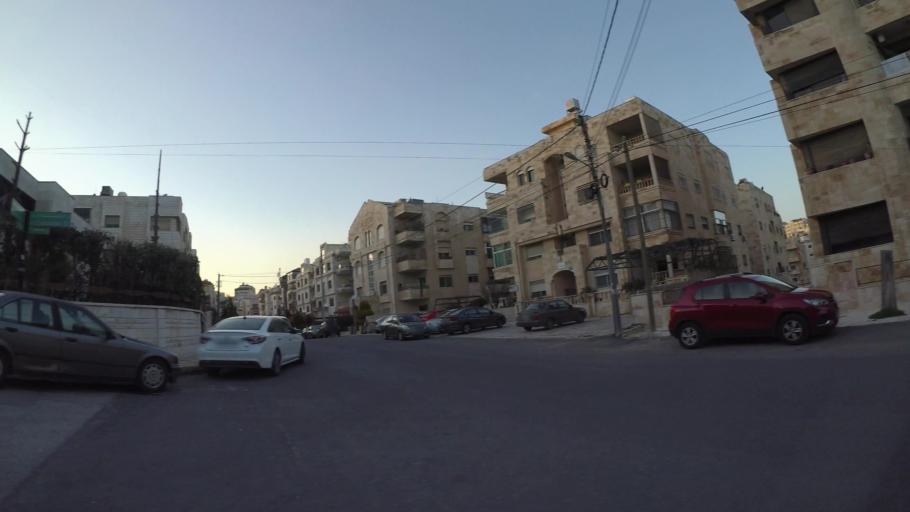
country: JO
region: Amman
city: Al Jubayhah
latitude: 31.9880
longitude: 35.8807
